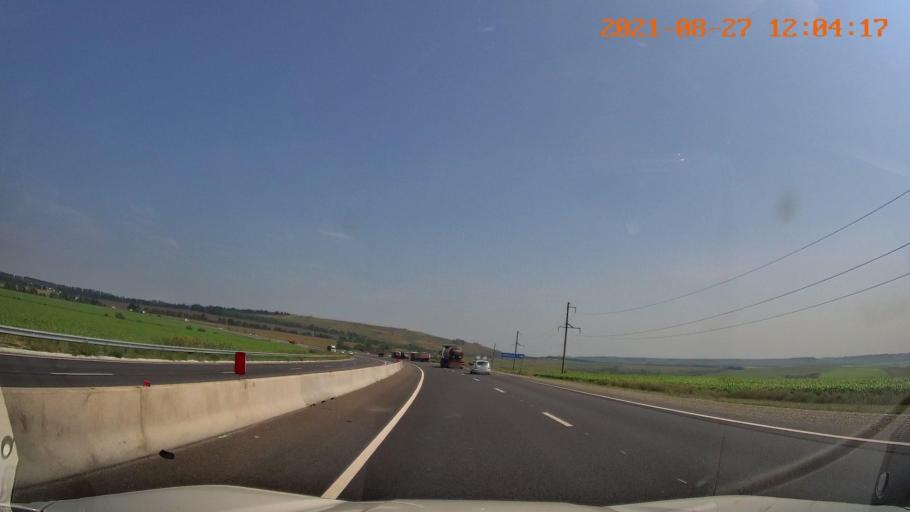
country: RU
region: Stavropol'skiy
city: Tatarka
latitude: 44.9535
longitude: 41.9837
